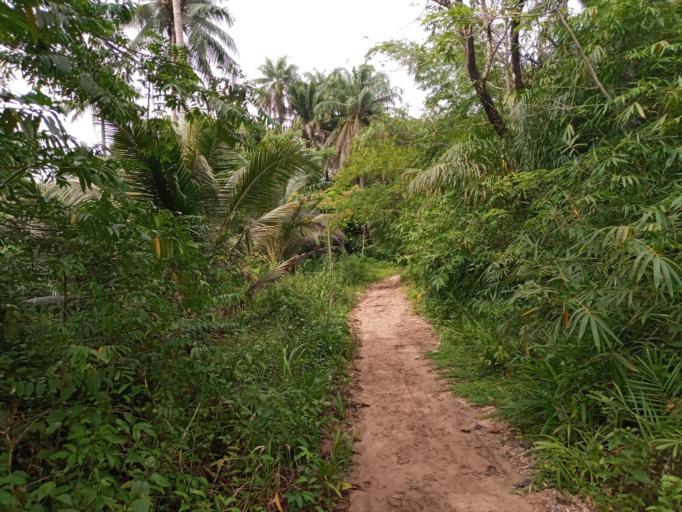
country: SL
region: Southern Province
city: Bonthe
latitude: 7.5120
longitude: -12.5485
